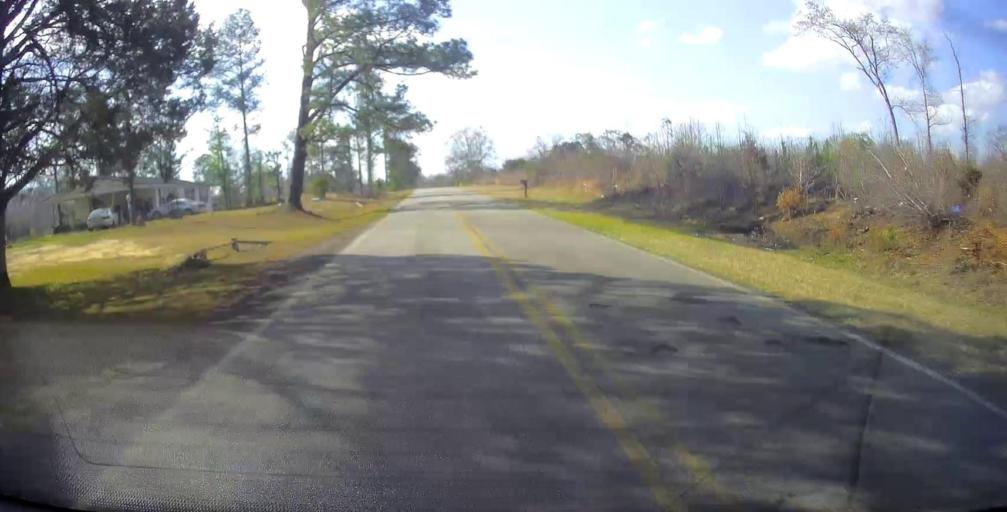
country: US
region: Georgia
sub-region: Wilkinson County
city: Irwinton
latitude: 32.6344
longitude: -83.1207
